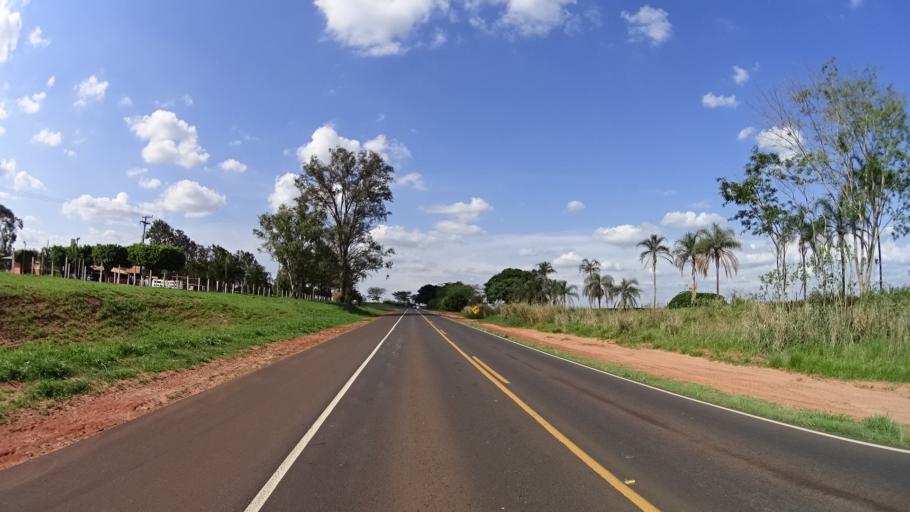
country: BR
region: Sao Paulo
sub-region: Guapiacu
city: Guapiacu
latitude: -20.9979
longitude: -49.2116
